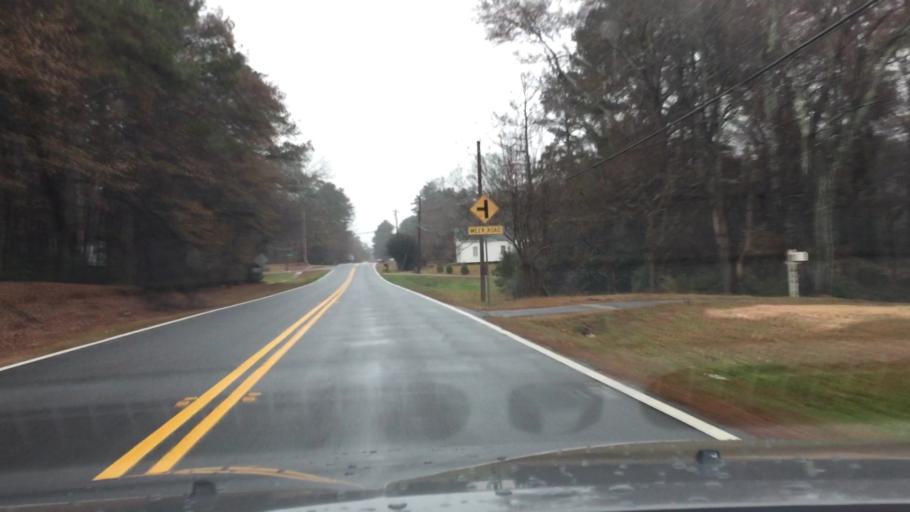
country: US
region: Georgia
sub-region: Cobb County
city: Powder Springs
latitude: 33.8850
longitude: -84.6764
